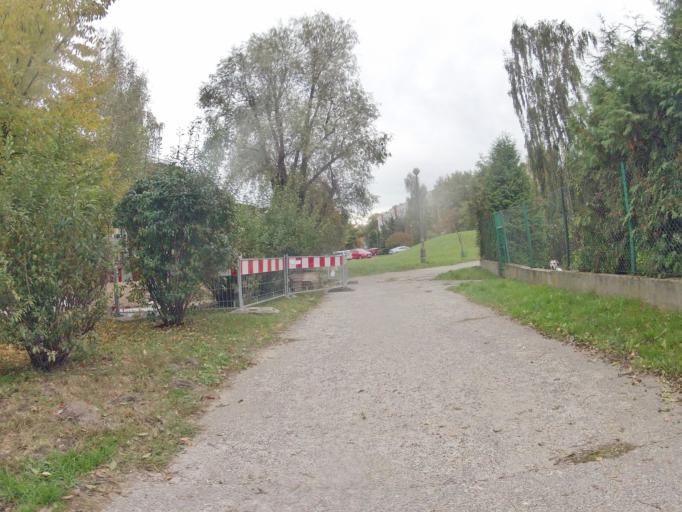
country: PL
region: Lesser Poland Voivodeship
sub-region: Krakow
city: Krakow
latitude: 50.0923
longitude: 19.9495
